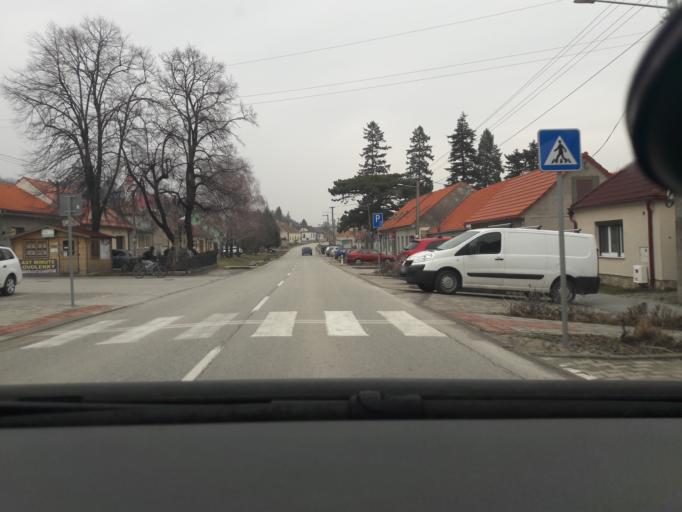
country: SK
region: Trnavsky
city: Smolenice
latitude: 48.5066
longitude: 17.4308
